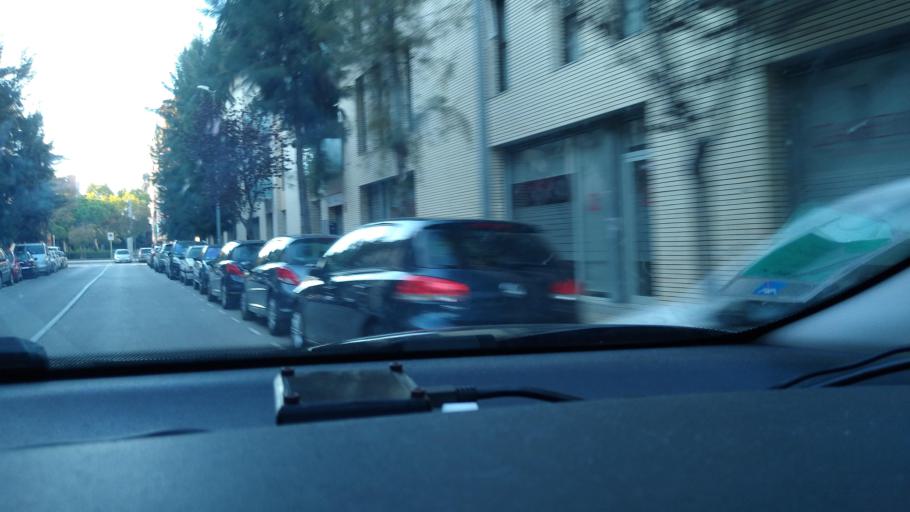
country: ES
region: Catalonia
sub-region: Provincia de Barcelona
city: Sant Joan Despi
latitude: 41.3590
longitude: 2.0610
